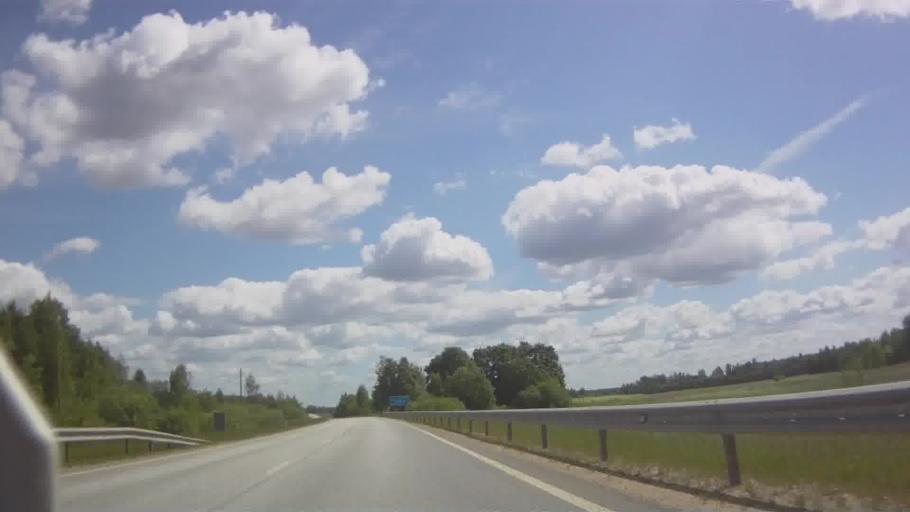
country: LV
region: Livani
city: Livani
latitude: 56.5248
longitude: 26.4138
